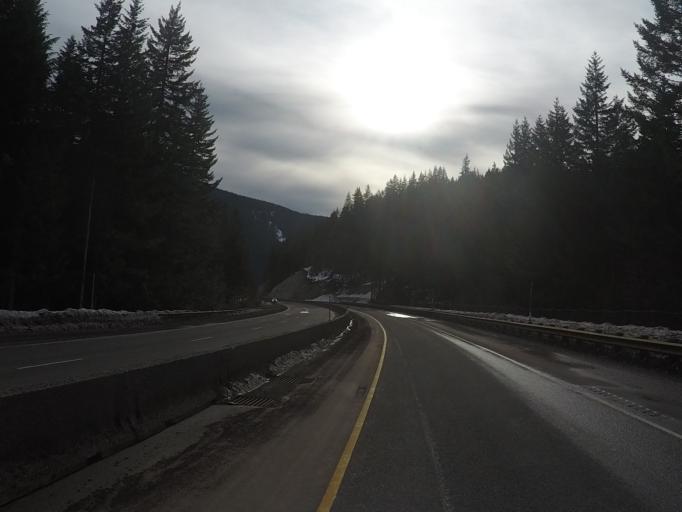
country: US
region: Oregon
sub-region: Clackamas County
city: Mount Hood Village
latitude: 45.3115
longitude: -121.8013
